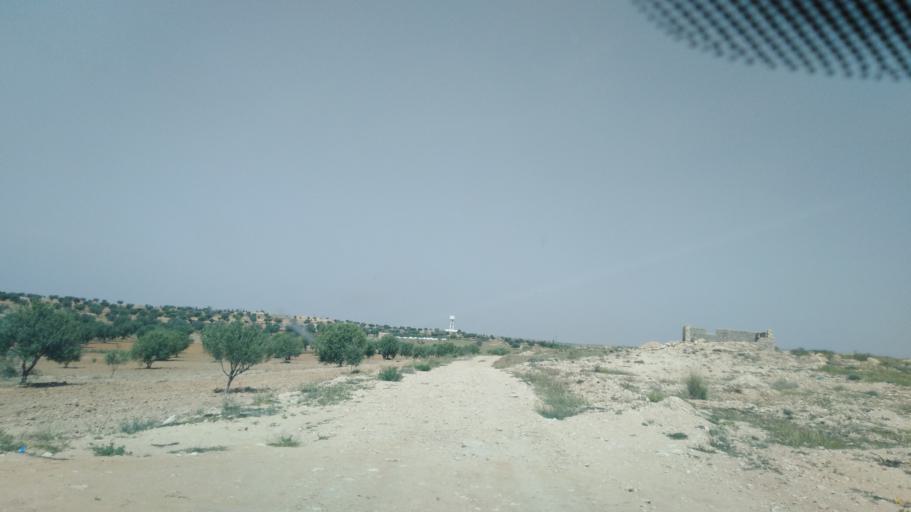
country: TN
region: Safaqis
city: Sfax
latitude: 34.7475
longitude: 10.5681
